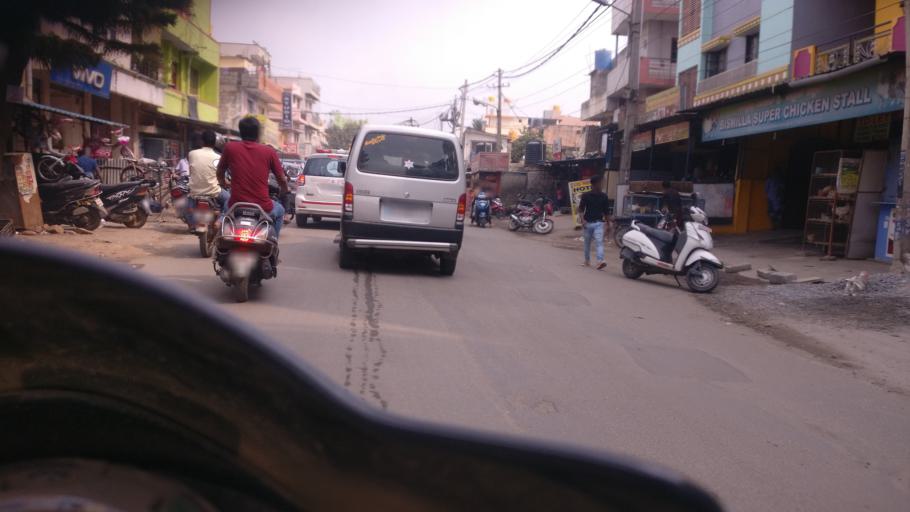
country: IN
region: Karnataka
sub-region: Bangalore Urban
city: Bangalore
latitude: 12.8718
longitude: 77.6541
